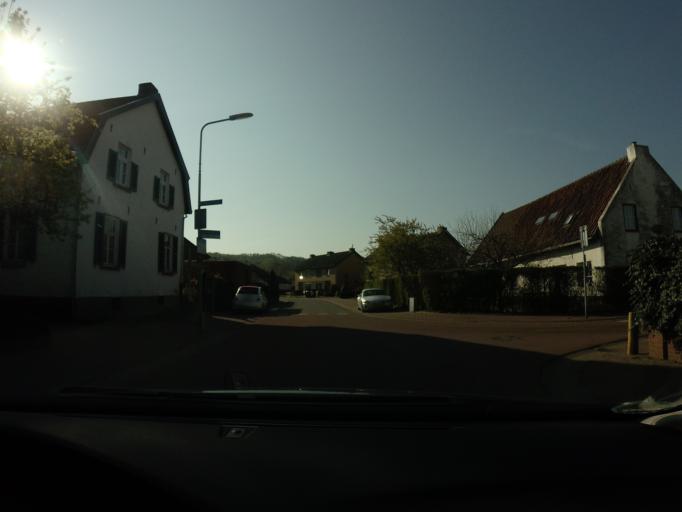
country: NL
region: Limburg
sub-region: Gemeente Meerssen
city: Meerssen
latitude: 50.9108
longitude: 5.7350
